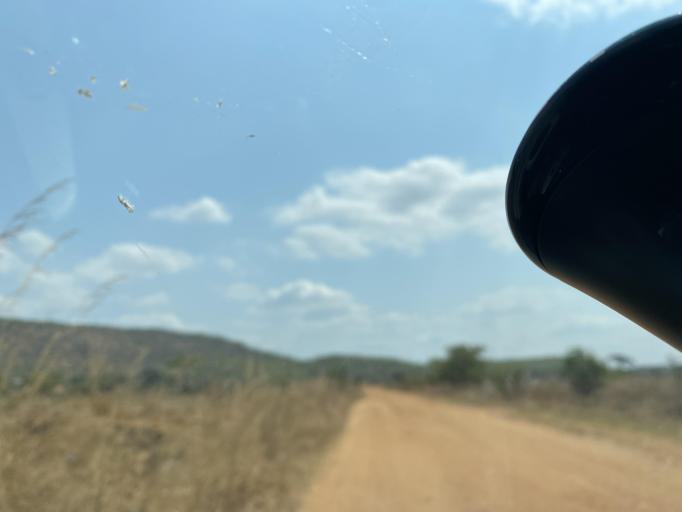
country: ZM
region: Lusaka
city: Chongwe
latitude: -15.6008
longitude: 28.7505
